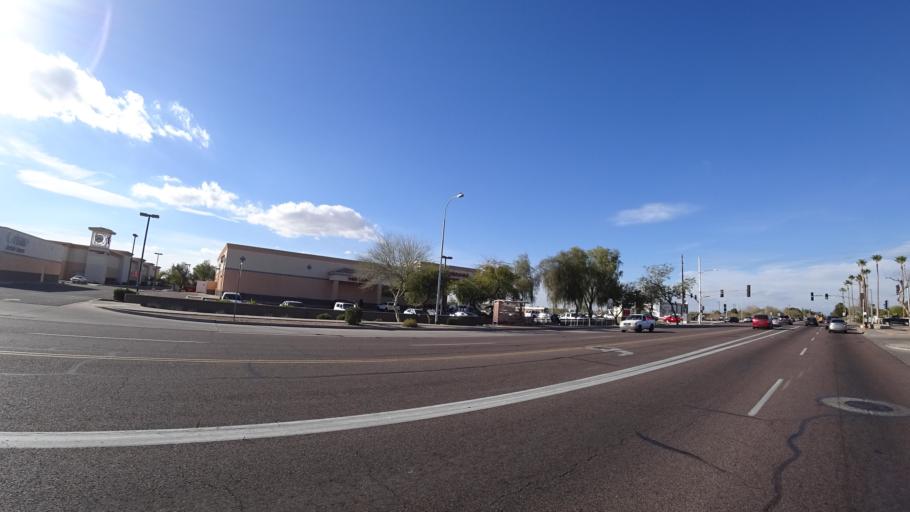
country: US
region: Arizona
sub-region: Maricopa County
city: Glendale
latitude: 33.5079
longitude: -112.2376
